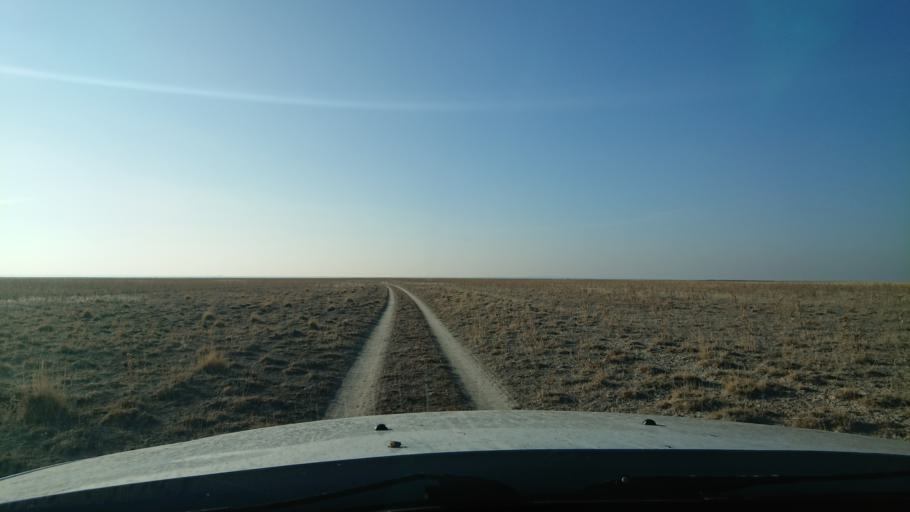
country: TR
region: Aksaray
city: Sultanhani
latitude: 38.3717
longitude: 33.5503
